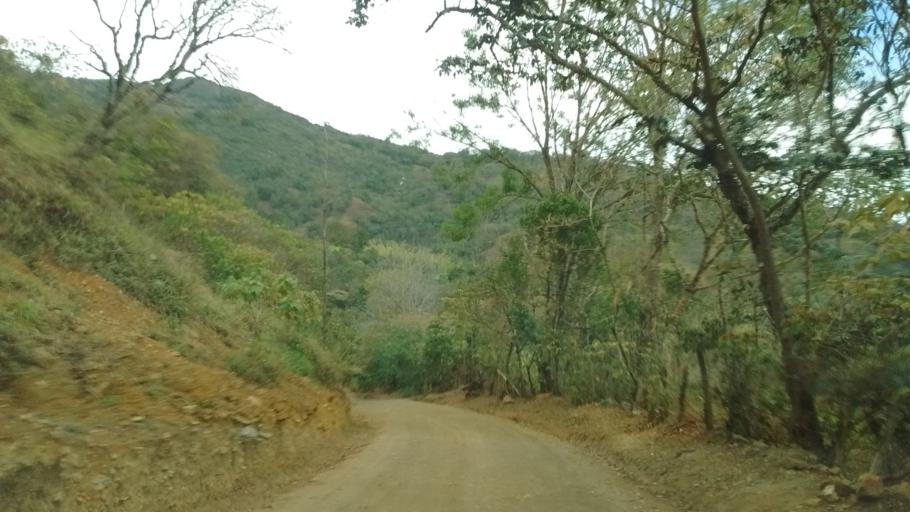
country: CO
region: Cauca
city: Almaguer
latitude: 1.8430
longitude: -76.9196
